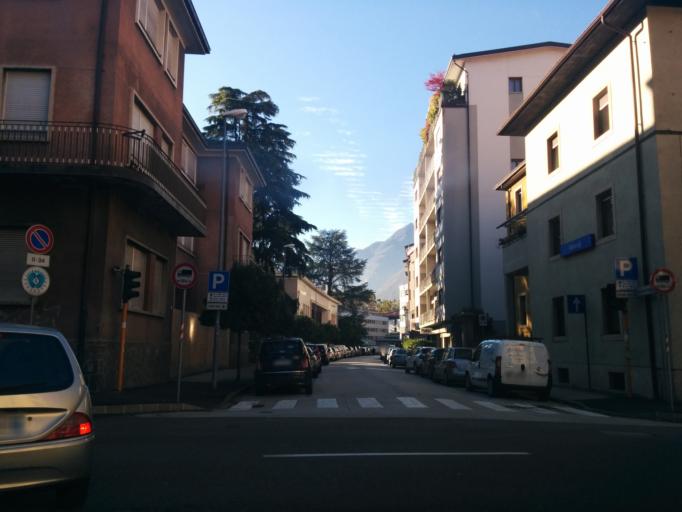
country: IT
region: Trentino-Alto Adige
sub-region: Provincia di Trento
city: Trento
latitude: 46.0726
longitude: 11.1239
